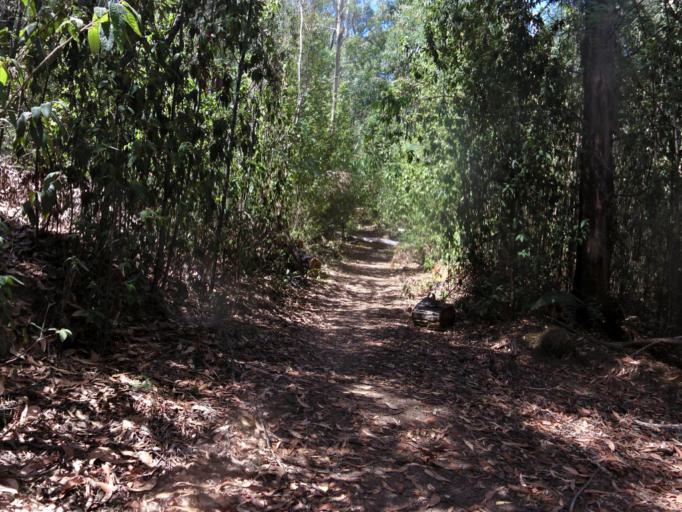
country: AU
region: Victoria
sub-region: Yarra Ranges
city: Healesville
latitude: -37.4068
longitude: 145.5633
